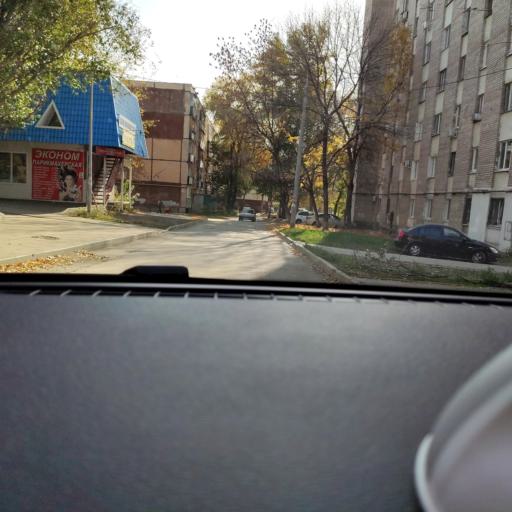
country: RU
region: Samara
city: Samara
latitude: 53.2545
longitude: 50.2426
